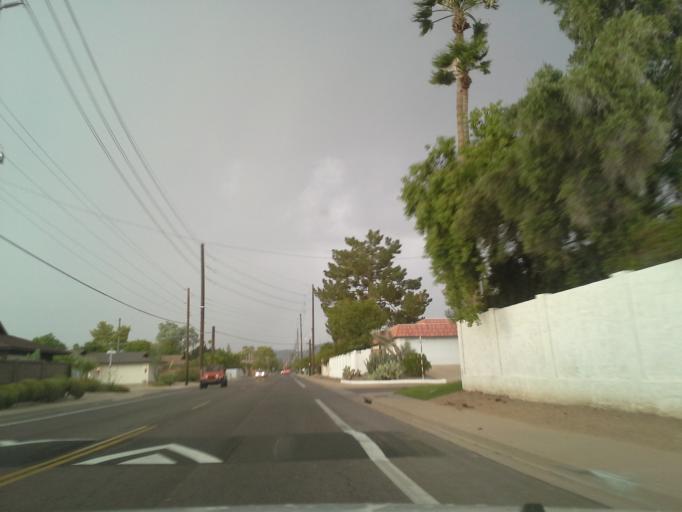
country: US
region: Arizona
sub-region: Maricopa County
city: Phoenix
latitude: 33.5336
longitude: -112.0911
